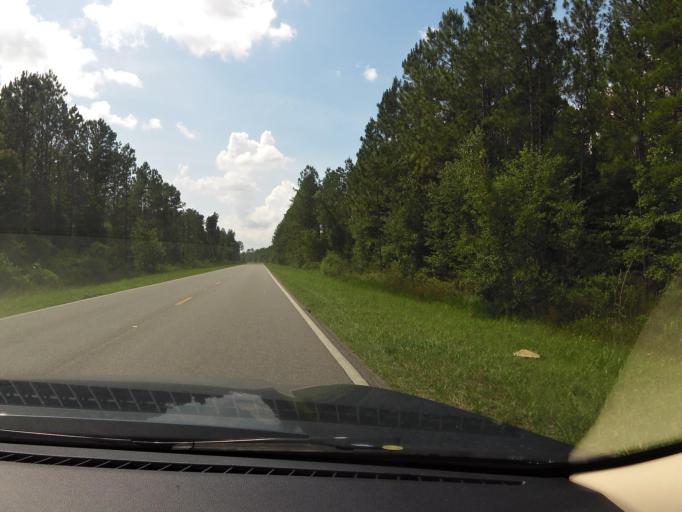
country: US
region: Florida
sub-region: Baker County
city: Macclenny
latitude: 30.2508
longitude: -82.0838
